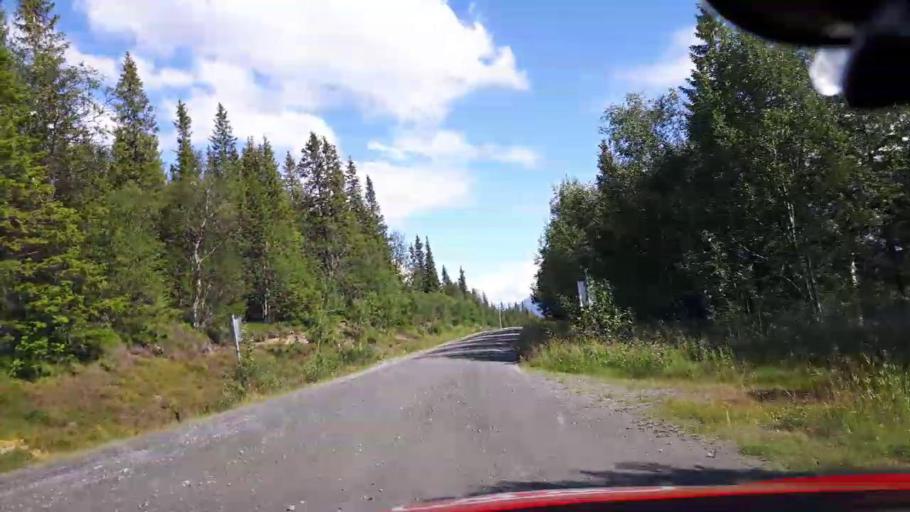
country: SE
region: Jaemtland
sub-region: Are Kommun
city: Are
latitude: 63.2197
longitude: 13.0512
